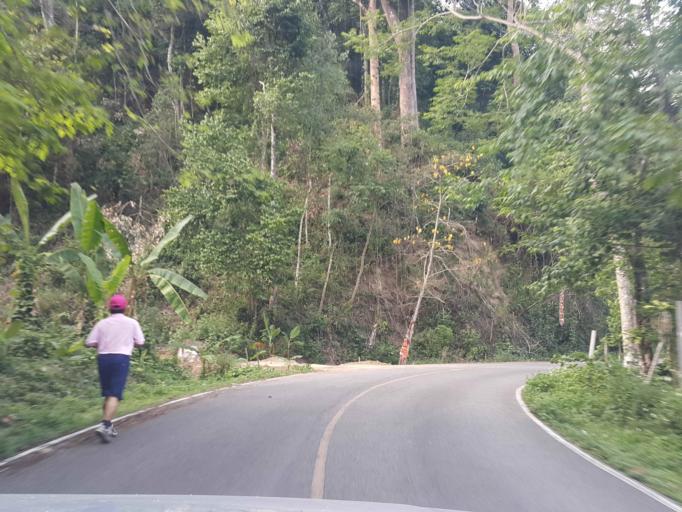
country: TH
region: Chiang Mai
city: Mae On
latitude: 18.9341
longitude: 99.3475
